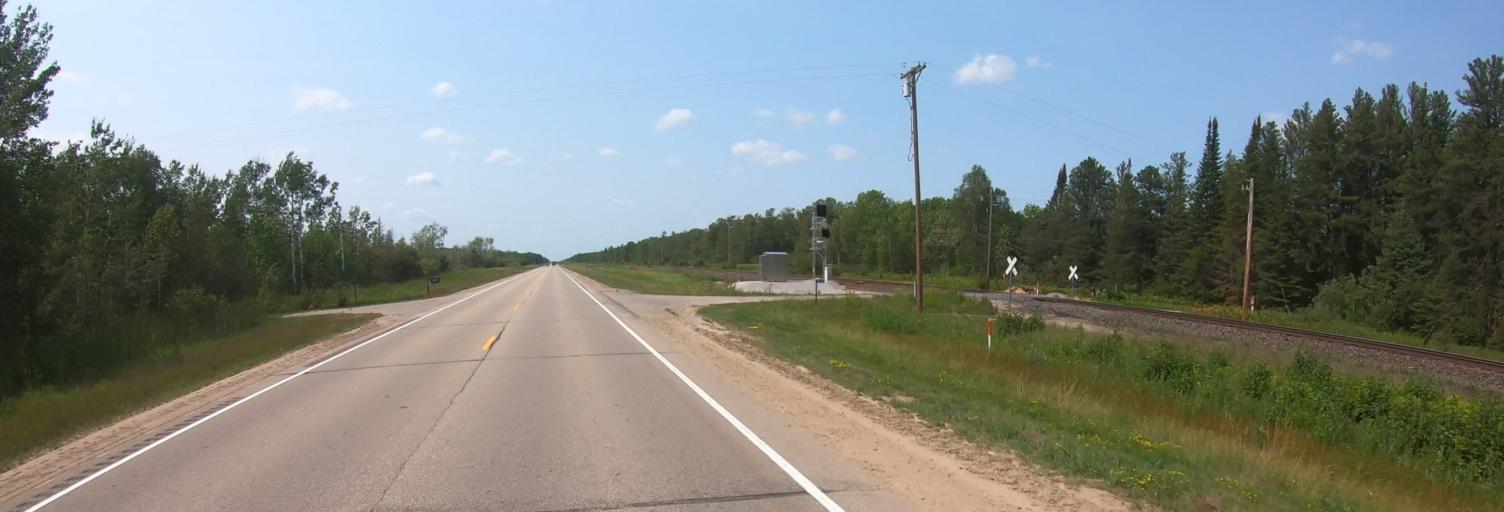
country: US
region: Minnesota
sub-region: Roseau County
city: Warroad
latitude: 48.7762
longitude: -94.9931
